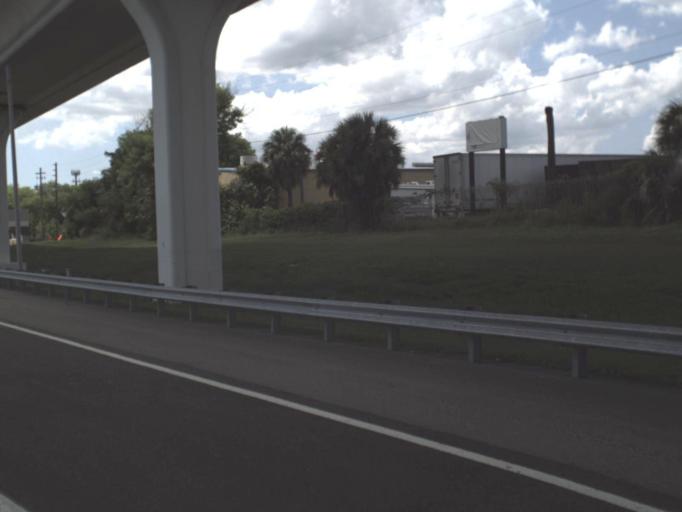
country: US
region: Florida
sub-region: Hillsborough County
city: Palm River-Clair Mel
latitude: 27.9503
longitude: -82.3773
